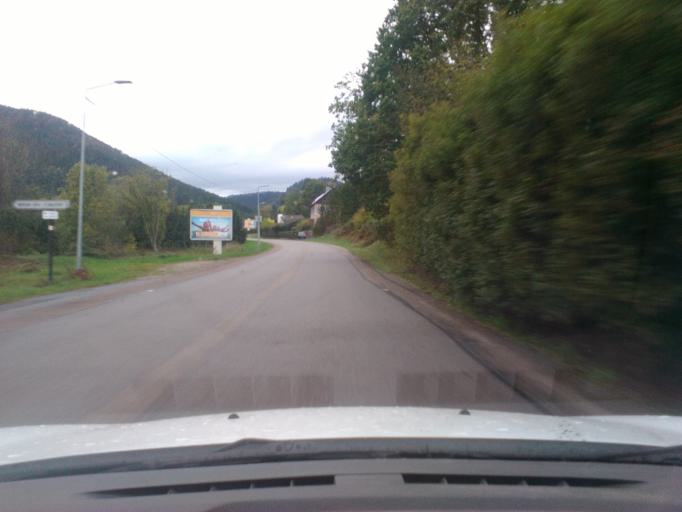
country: FR
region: Lorraine
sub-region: Departement des Vosges
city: Taintrux
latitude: 48.2773
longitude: 6.9029
